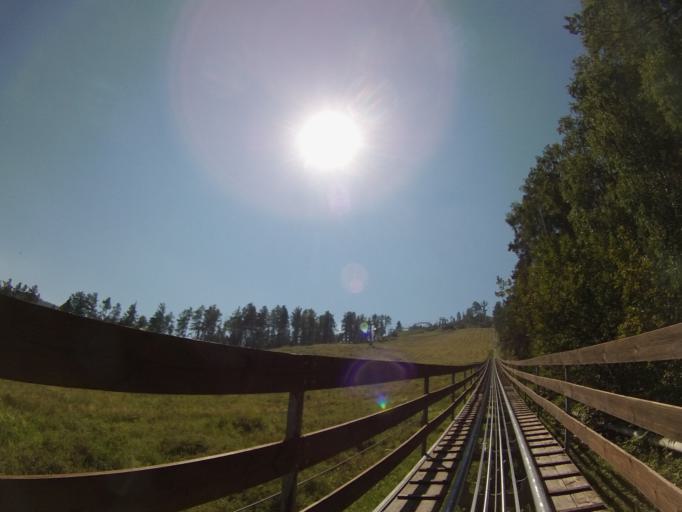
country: RU
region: Krasnoyarskiy
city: Krasnoyarsk
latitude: 55.9585
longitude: 92.7880
